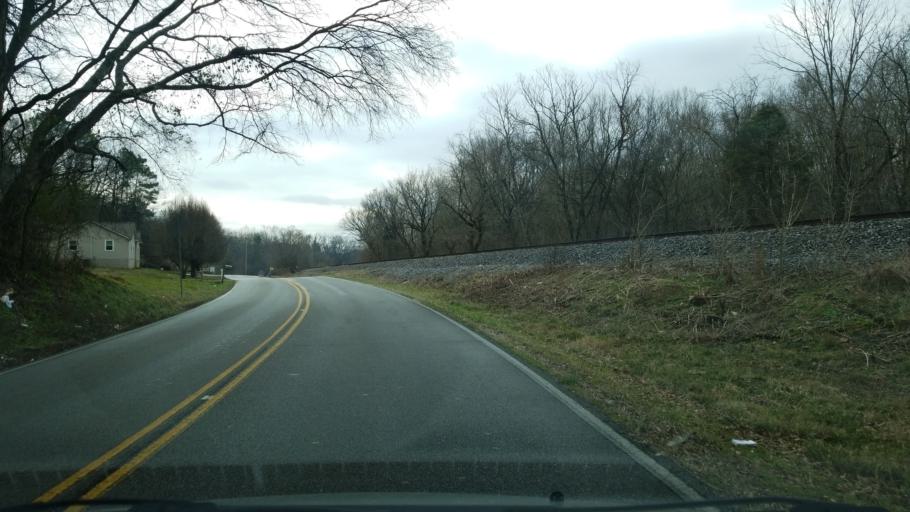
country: US
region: Tennessee
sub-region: Hamilton County
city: East Brainerd
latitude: 34.9807
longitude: -85.1463
